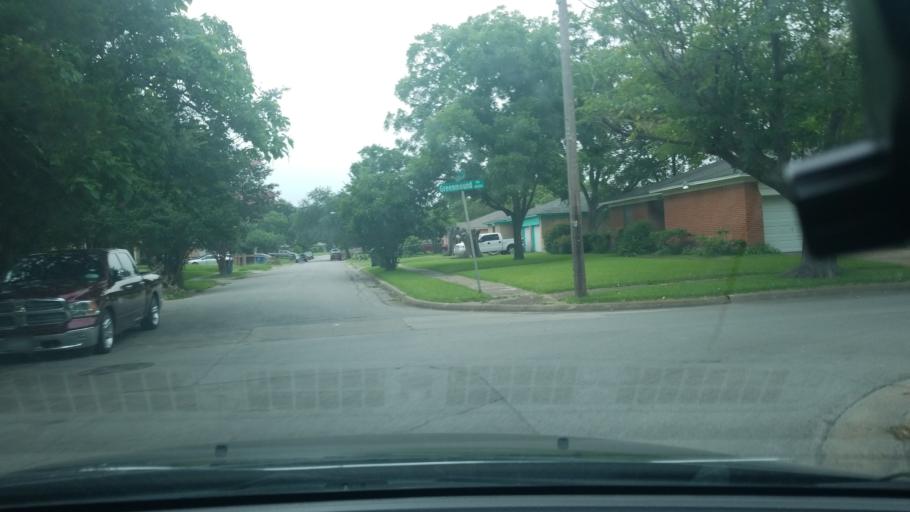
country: US
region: Texas
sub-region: Dallas County
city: Balch Springs
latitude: 32.7538
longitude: -96.6764
